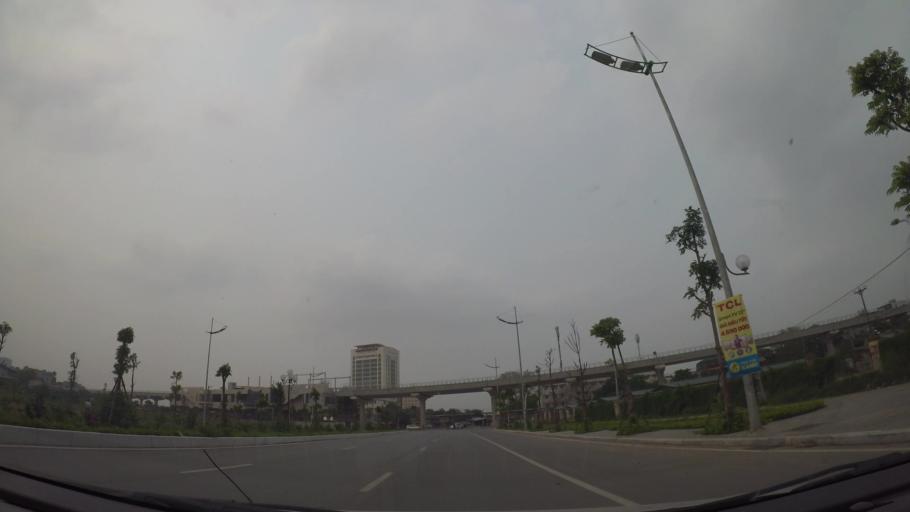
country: VN
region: Ha Noi
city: Cau Dien
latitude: 21.0510
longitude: 105.7358
